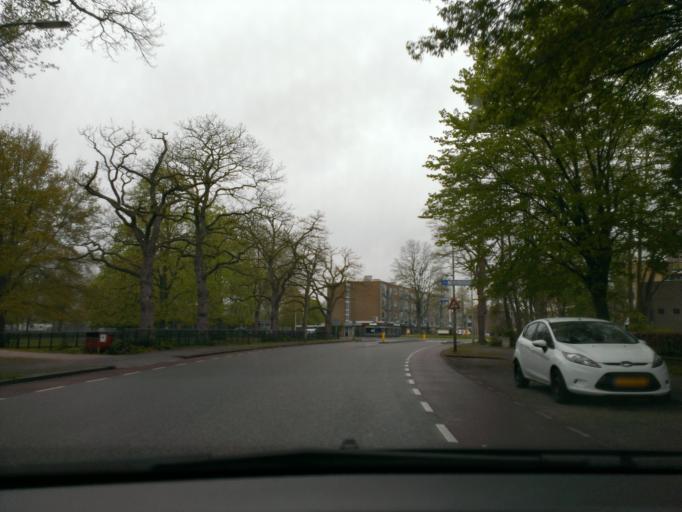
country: NL
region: Overijssel
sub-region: Gemeente Zwolle
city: Zwolle
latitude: 52.5200
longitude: 6.1068
